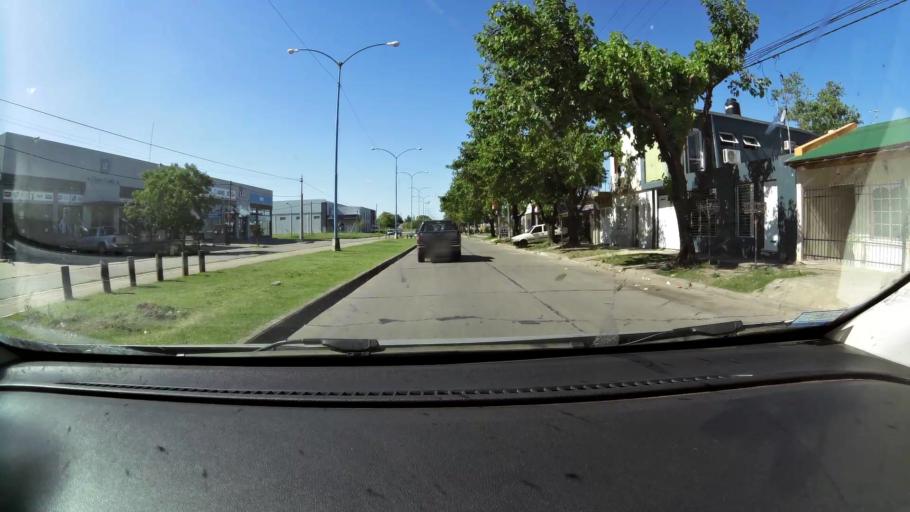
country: AR
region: Santa Fe
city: Rafaela
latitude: -31.2383
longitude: -61.4883
